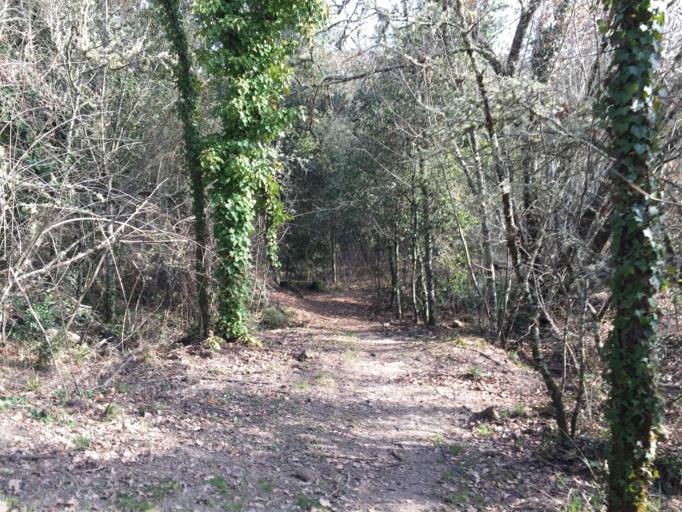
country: IT
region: Latium
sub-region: Provincia di Viterbo
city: Calcata Nuova
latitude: 42.2109
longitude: 12.4186
